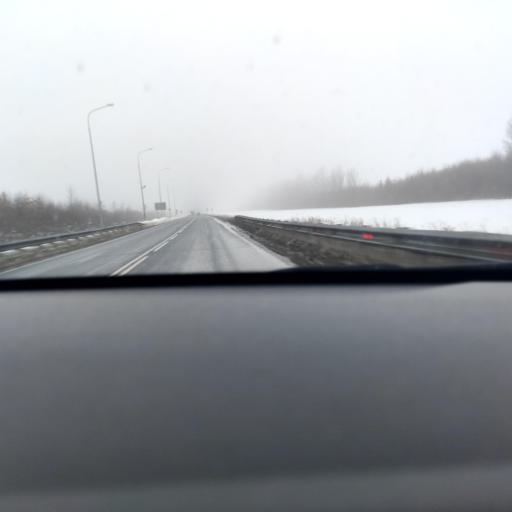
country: RU
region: Tatarstan
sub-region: Chistopol'skiy Rayon
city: Chistopol'
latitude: 55.3350
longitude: 50.4869
